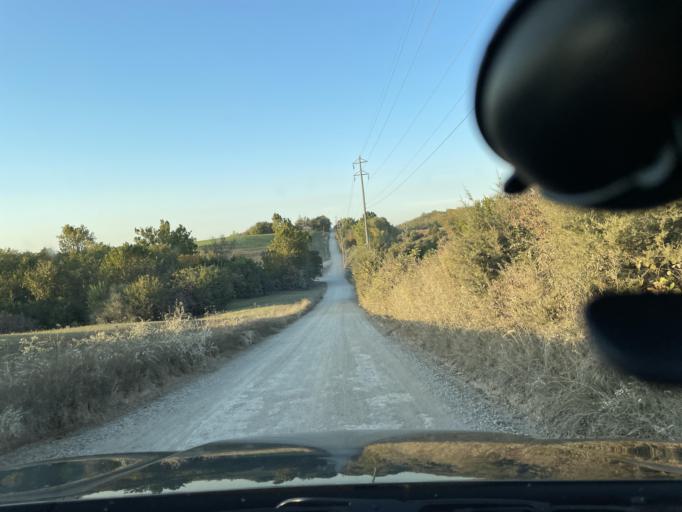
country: US
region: Missouri
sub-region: Andrew County
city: Savannah
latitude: 39.9285
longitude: -94.8612
